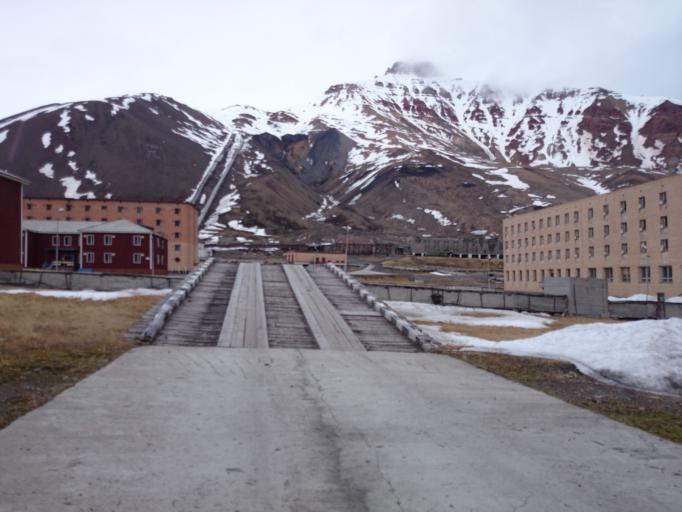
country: SJ
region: Svalbard
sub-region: Spitsbergen
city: Longyearbyen
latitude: 78.6551
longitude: 16.3246
